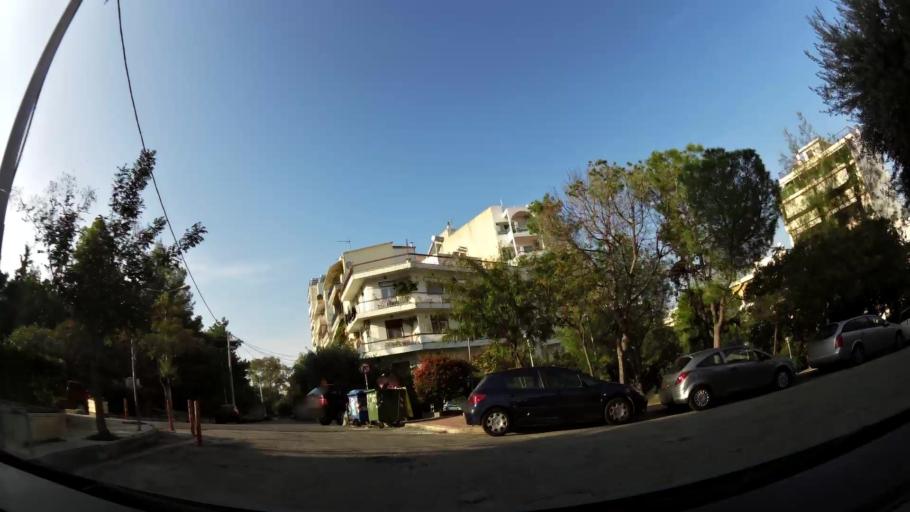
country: GR
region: Attica
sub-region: Nomarchia Athinas
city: Kaisariani
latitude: 37.9703
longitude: 23.7712
